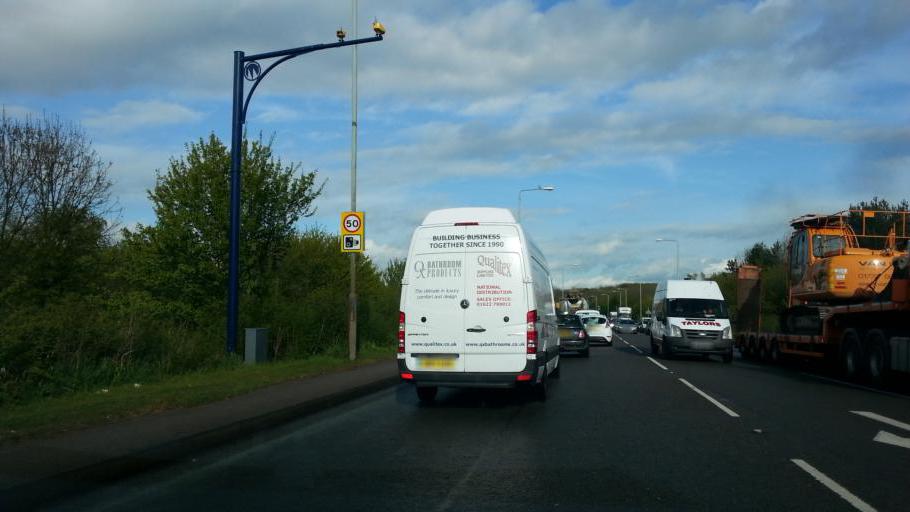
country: GB
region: England
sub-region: Nottinghamshire
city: Sutton in Ashfield
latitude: 53.1135
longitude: -1.2656
